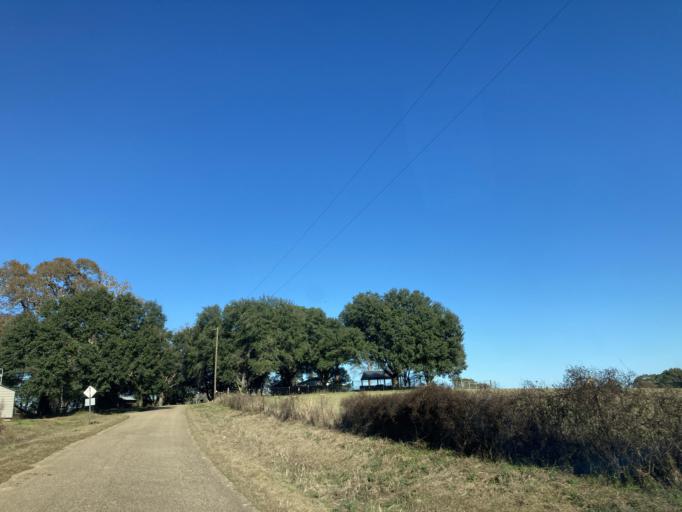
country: US
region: Mississippi
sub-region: Lamar County
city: Sumrall
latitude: 31.3490
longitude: -89.6064
